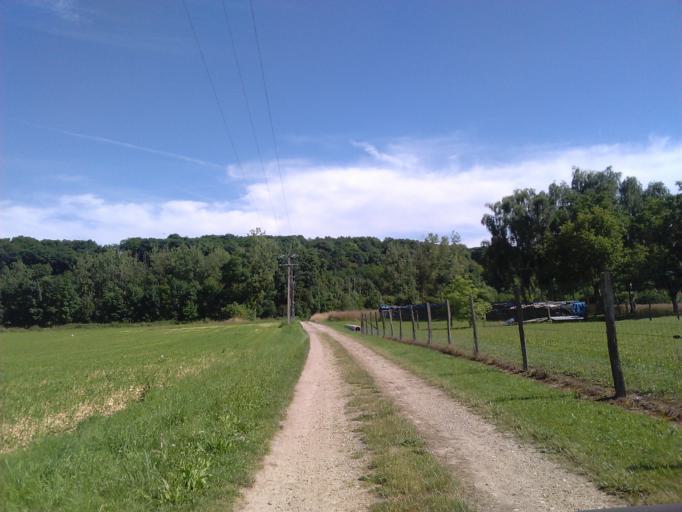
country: FR
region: Centre
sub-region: Departement du Loir-et-Cher
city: Villiers-sur-Loir
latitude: 47.8253
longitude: 0.9730
